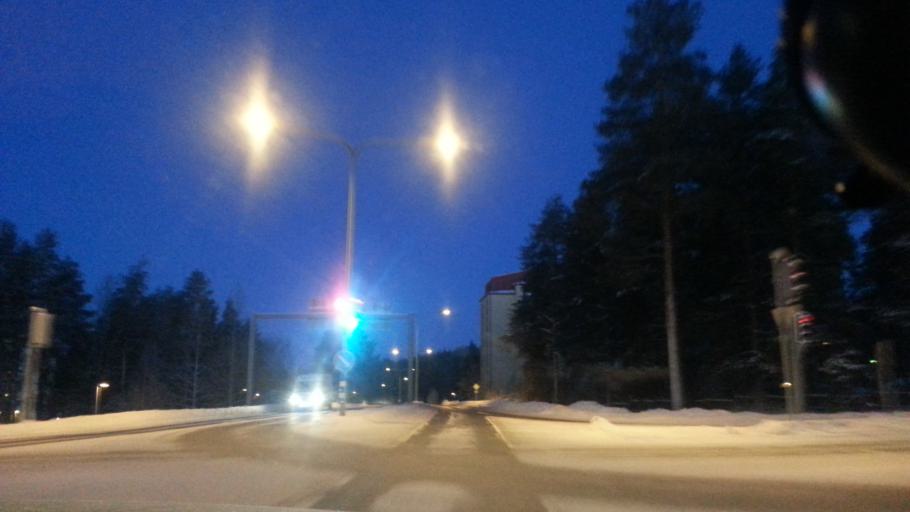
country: FI
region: Lapland
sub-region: Rovaniemi
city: Rovaniemi
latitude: 66.4975
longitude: 25.7569
